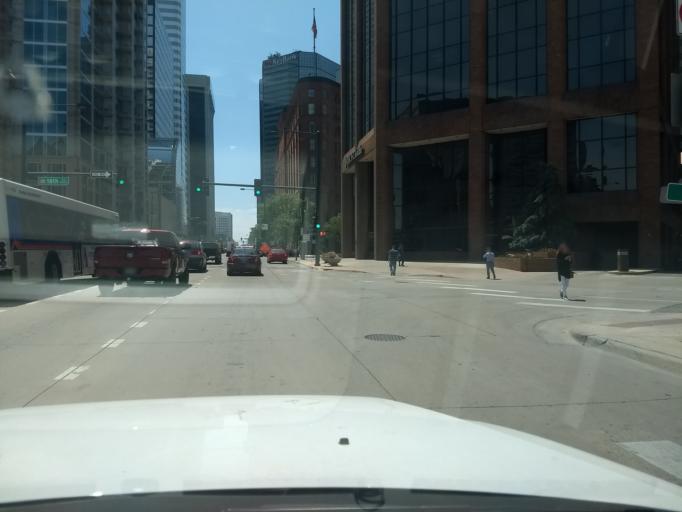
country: US
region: Colorado
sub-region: Denver County
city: Denver
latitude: 39.7455
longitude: -104.9875
